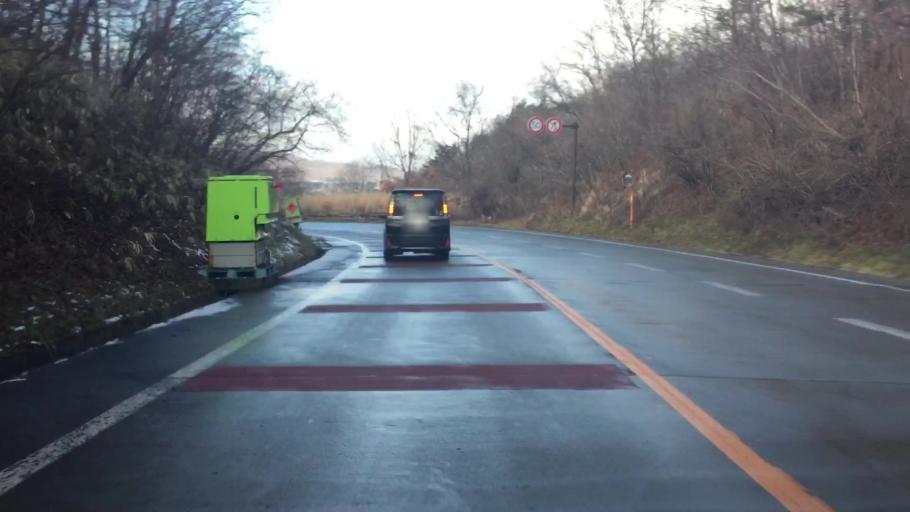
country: JP
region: Nagano
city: Saku
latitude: 36.3047
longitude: 138.6472
